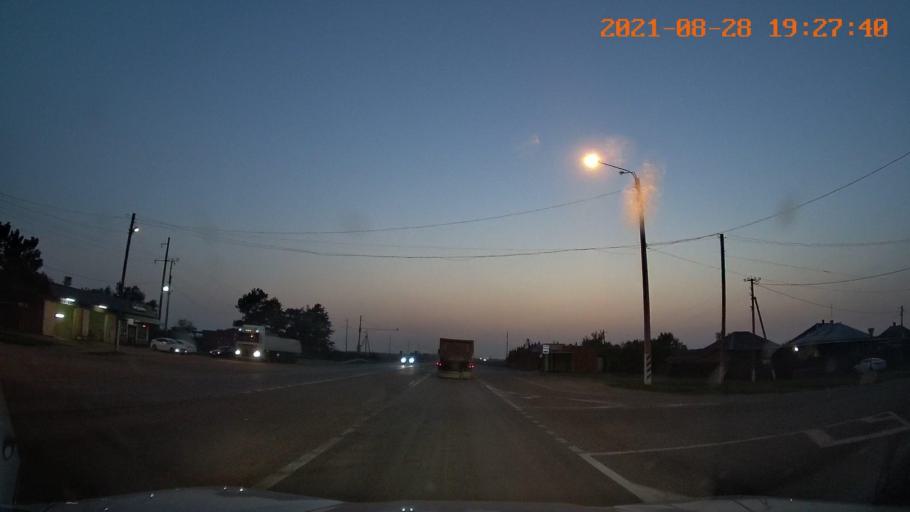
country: RU
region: Adygeya
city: Ponezhukay
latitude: 44.8787
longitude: 39.3812
